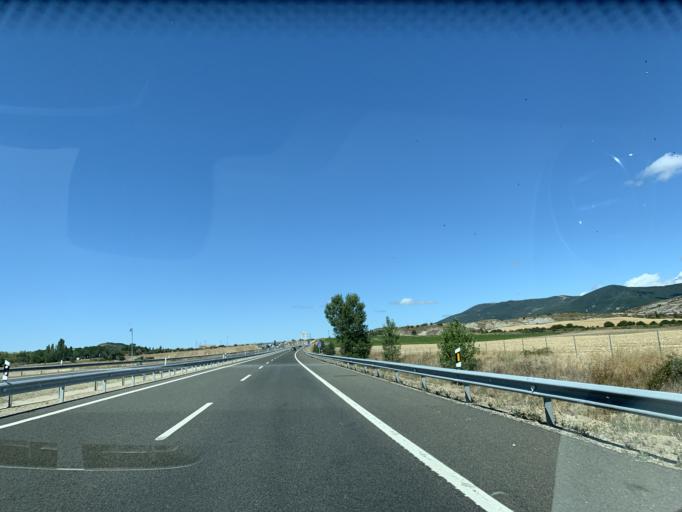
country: ES
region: Aragon
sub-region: Provincia de Huesca
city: Sabinanigo
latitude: 42.5476
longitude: -0.4199
